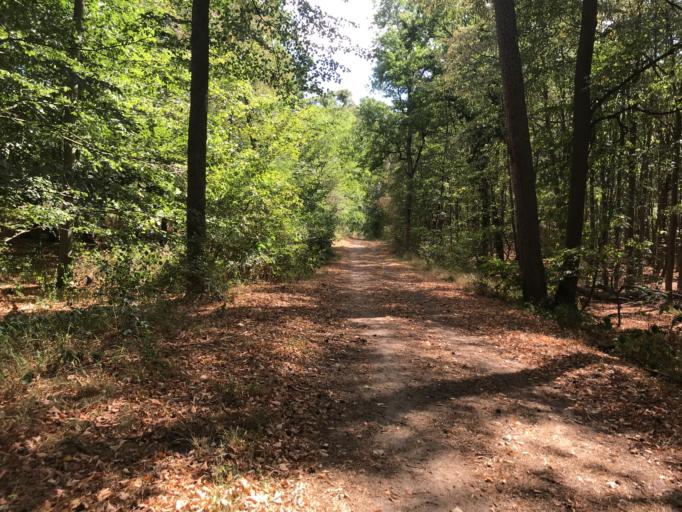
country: DE
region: Rheinland-Pfalz
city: Budenheim
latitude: 50.0130
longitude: 8.1608
